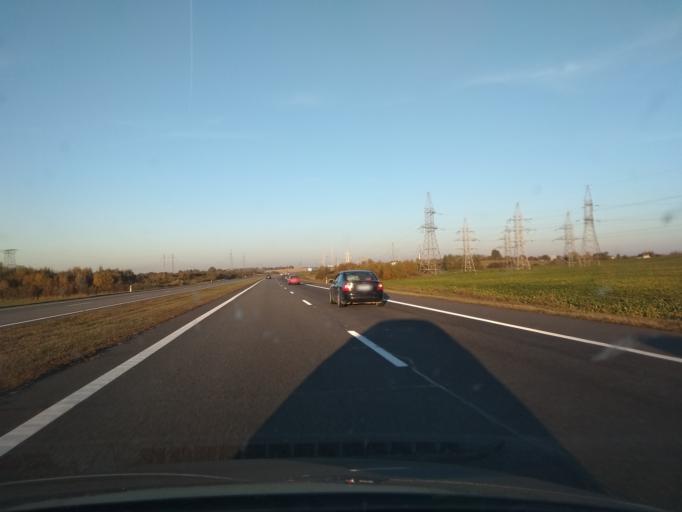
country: BY
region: Brest
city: Baranovichi
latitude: 53.1722
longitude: 26.0025
